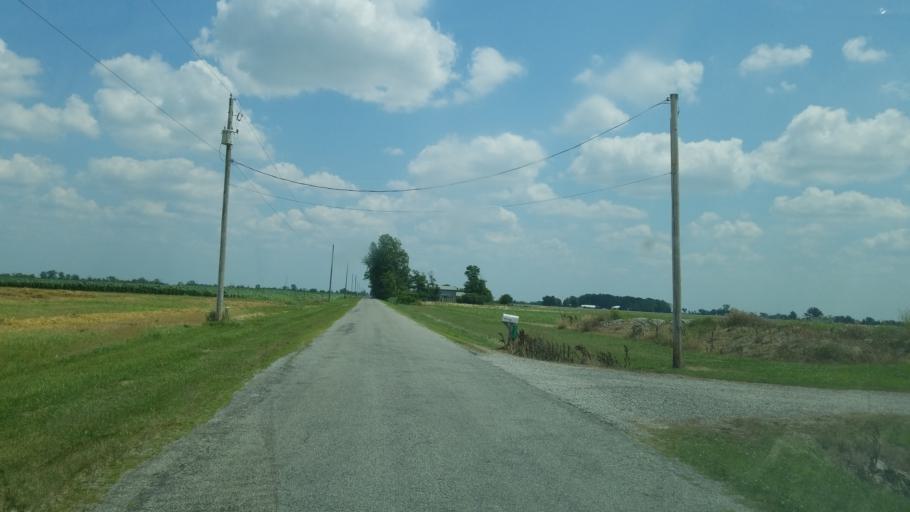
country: US
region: Ohio
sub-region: Henry County
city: Deshler
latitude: 41.2552
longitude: -83.8541
